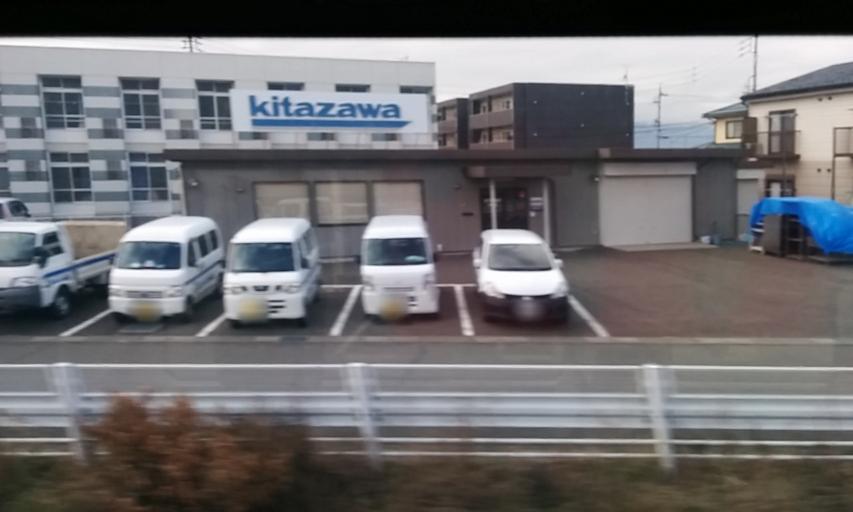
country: JP
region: Nagano
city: Matsumoto
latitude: 36.1904
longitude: 137.9621
